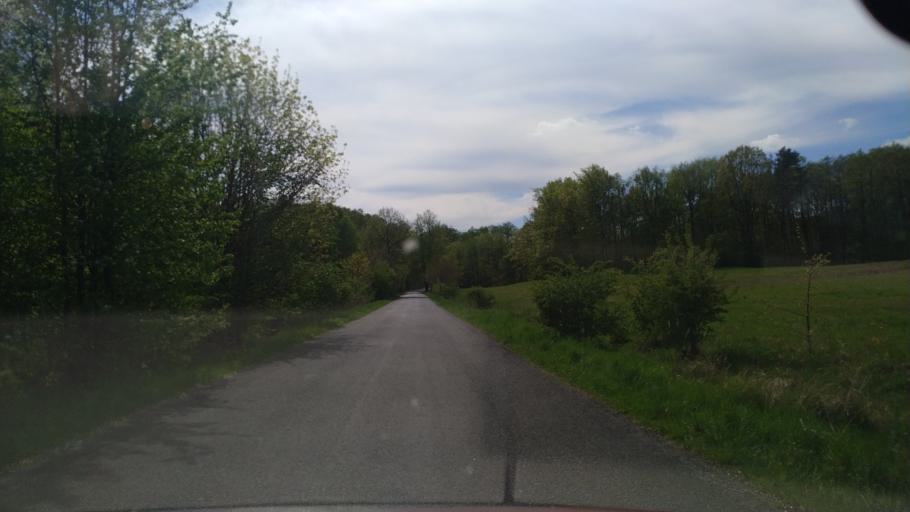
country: PL
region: West Pomeranian Voivodeship
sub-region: Powiat walecki
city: Miroslawiec
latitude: 53.3472
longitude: 16.2642
